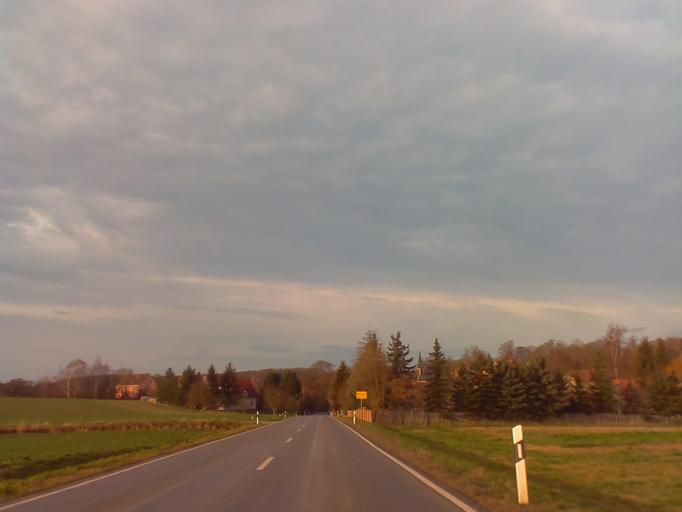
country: DE
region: Thuringia
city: Hummelshain
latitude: 50.7659
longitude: 11.6363
